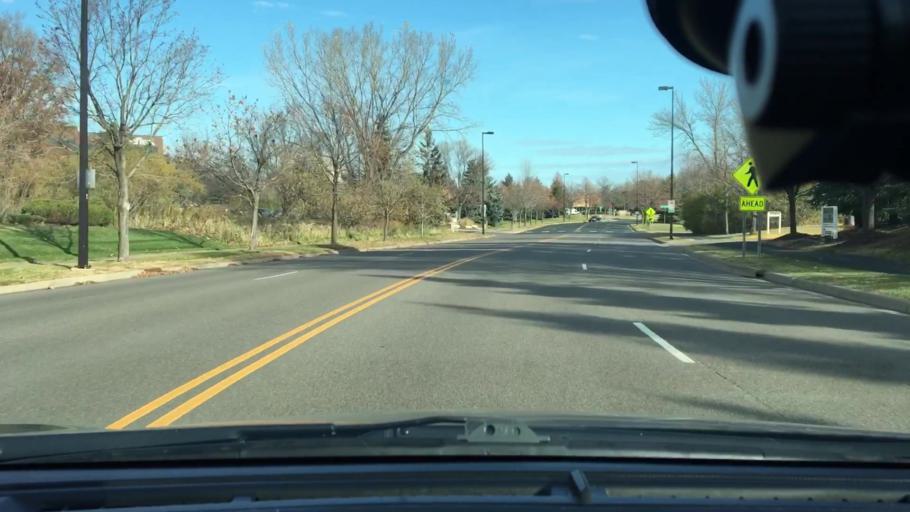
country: US
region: Minnesota
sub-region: Hennepin County
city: Maple Grove
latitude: 45.0693
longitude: -93.4432
